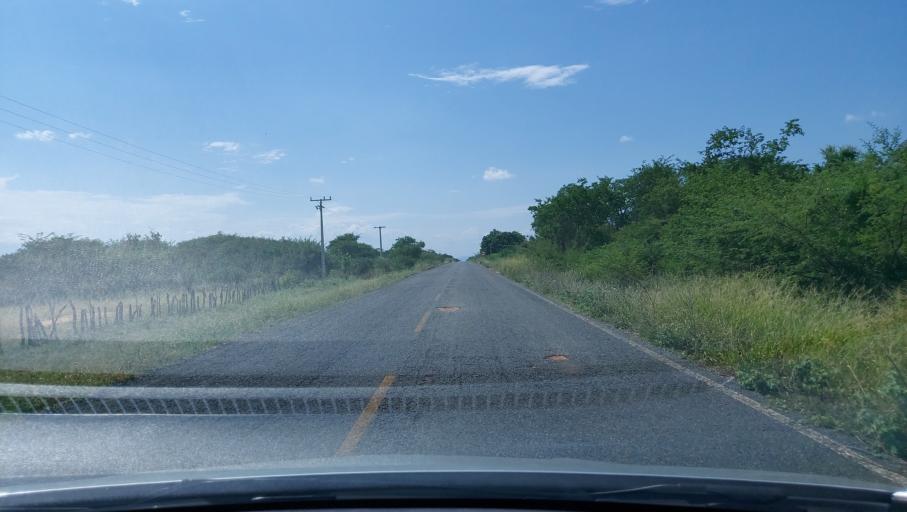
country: BR
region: Bahia
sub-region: Oliveira Dos Brejinhos
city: Beira Rio
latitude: -12.1543
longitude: -42.5523
